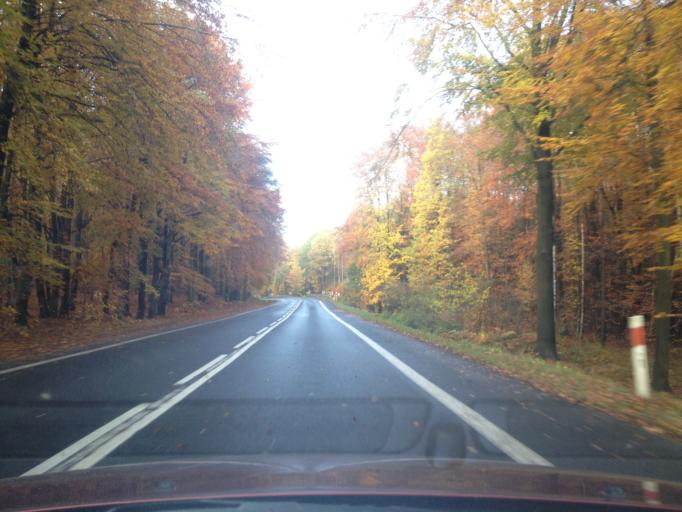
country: PL
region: Lower Silesian Voivodeship
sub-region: Powiat lubanski
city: Siekierczyn
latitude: 51.1596
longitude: 15.1488
